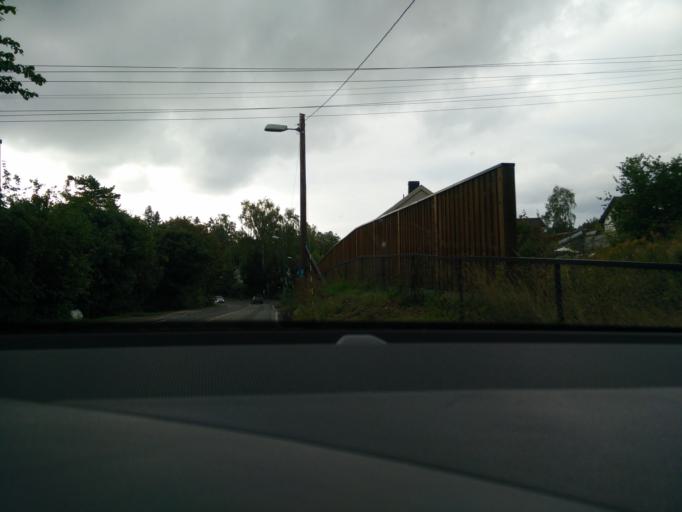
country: NO
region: Akershus
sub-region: Baerum
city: Lysaker
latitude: 59.9197
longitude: 10.6287
